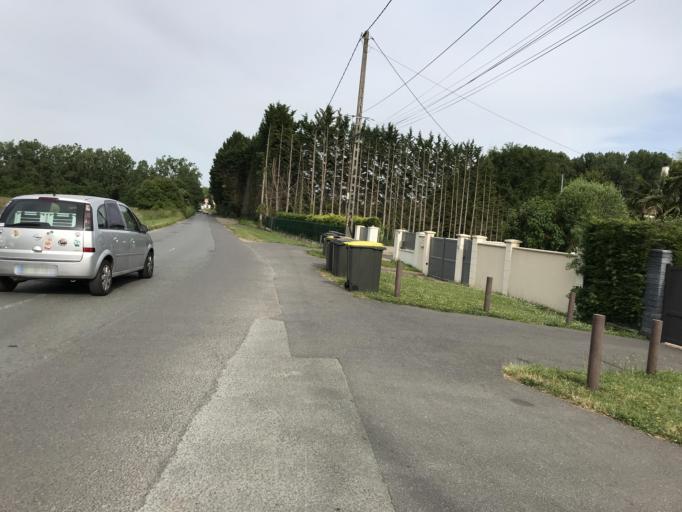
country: FR
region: Ile-de-France
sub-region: Departement de l'Essonne
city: Longpont-sur-Orge
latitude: 48.6262
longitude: 2.2929
